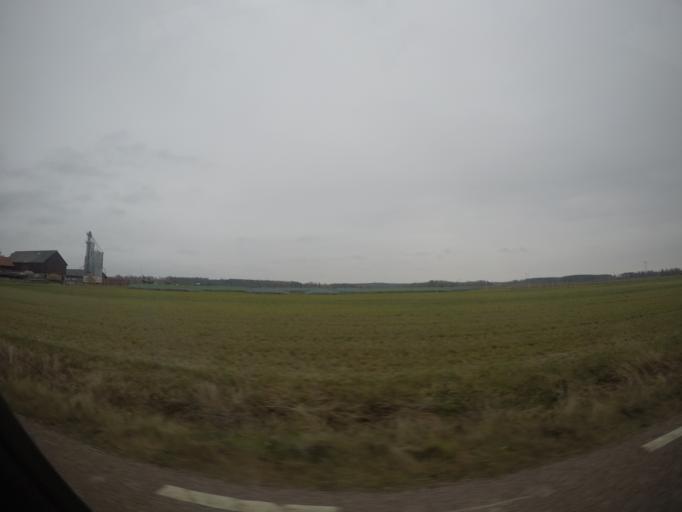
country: SE
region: Vaestmanland
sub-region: Kopings Kommun
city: Koping
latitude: 59.5572
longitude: 16.0968
